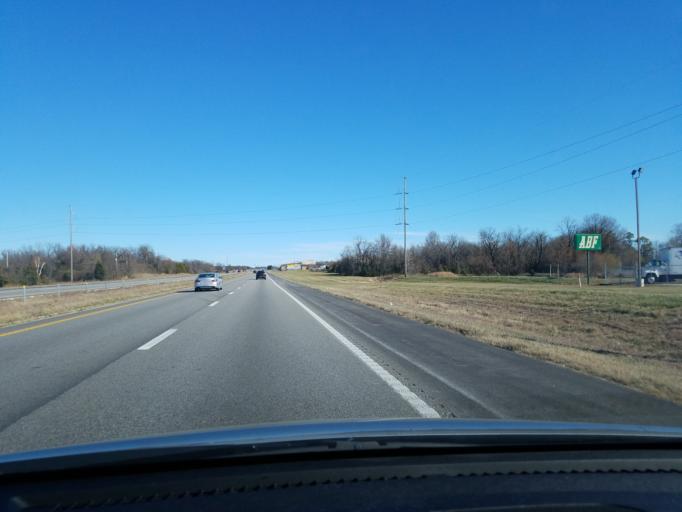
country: US
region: Missouri
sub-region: Greene County
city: Strafford
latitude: 37.2550
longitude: -93.1689
